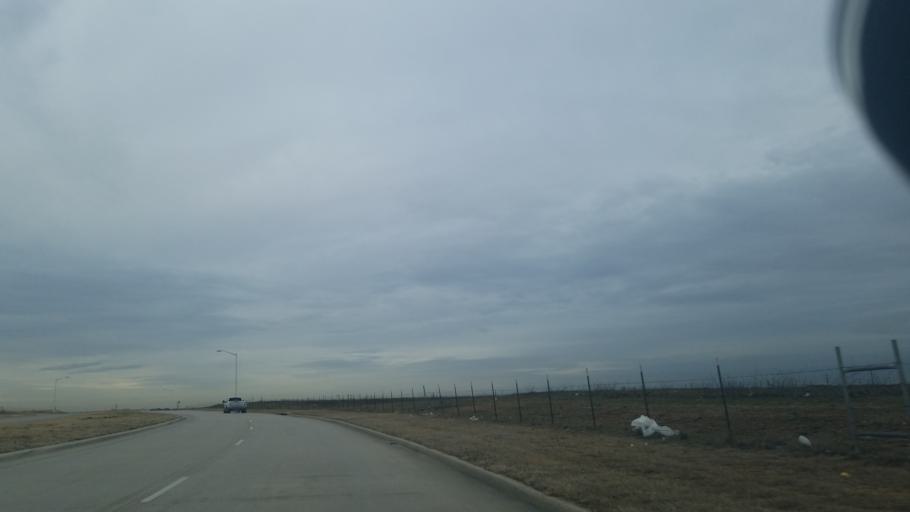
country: US
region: Texas
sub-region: Denton County
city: Denton
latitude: 33.2135
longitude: -97.1844
